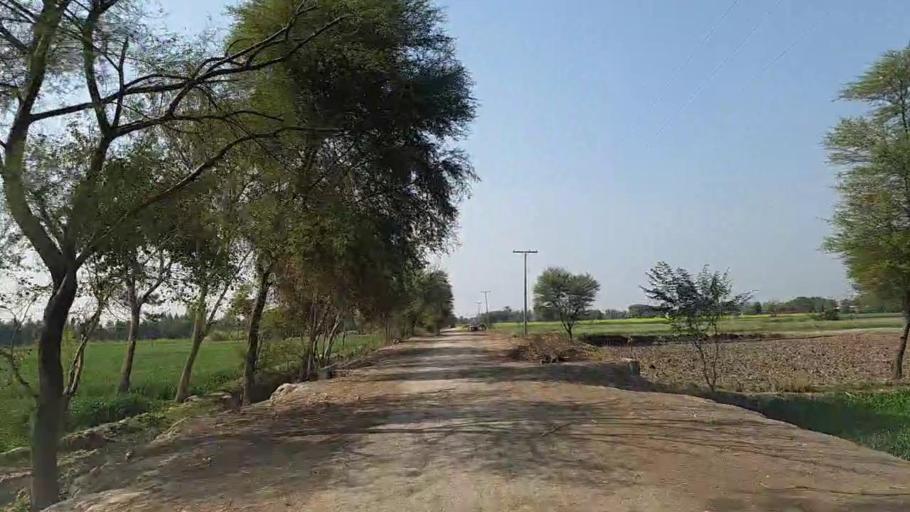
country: PK
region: Sindh
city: Nawabshah
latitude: 26.2475
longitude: 68.4797
